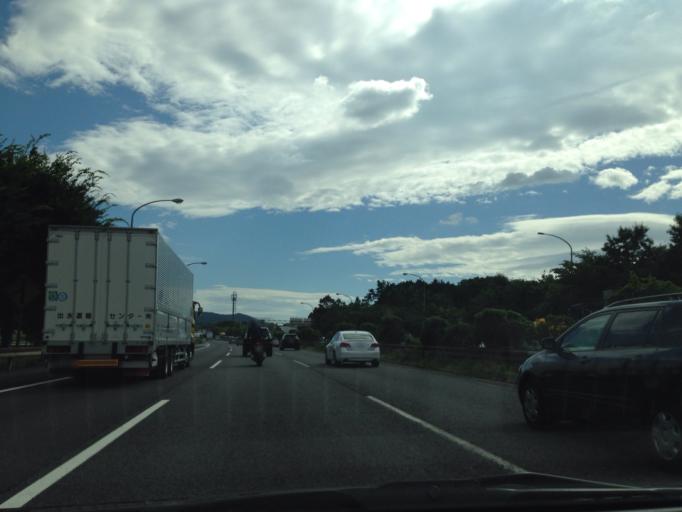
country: JP
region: Shizuoka
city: Gotemba
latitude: 35.3122
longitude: 138.9642
